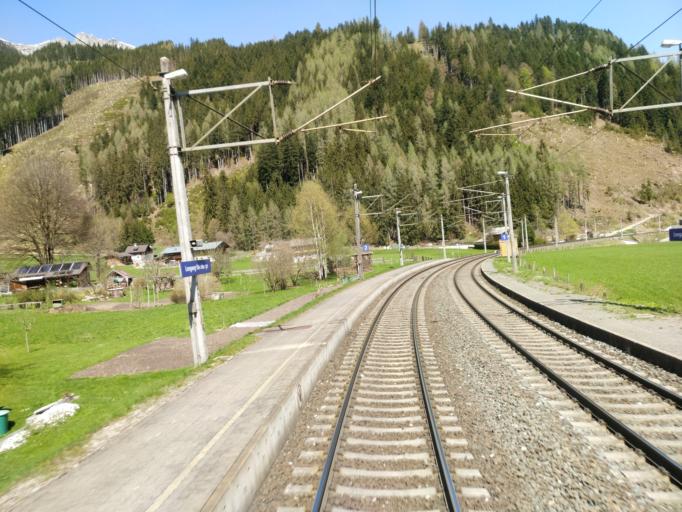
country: AT
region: Salzburg
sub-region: Politischer Bezirk Zell am See
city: Leogang
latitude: 47.4454
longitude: 12.7688
